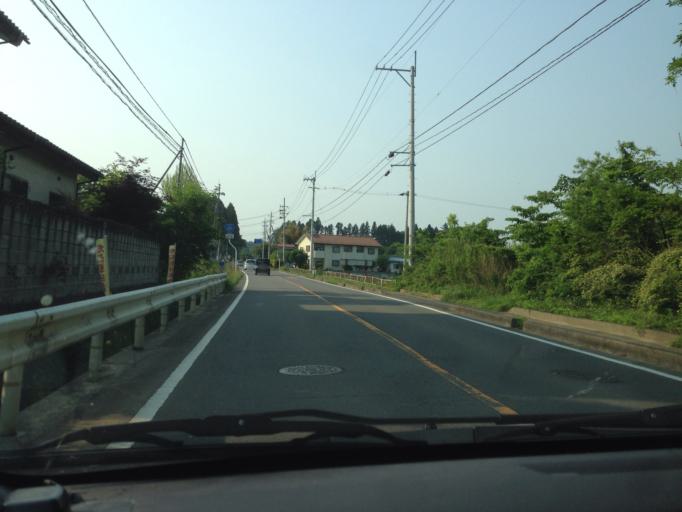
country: JP
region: Tochigi
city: Kuroiso
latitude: 37.0973
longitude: 140.1976
